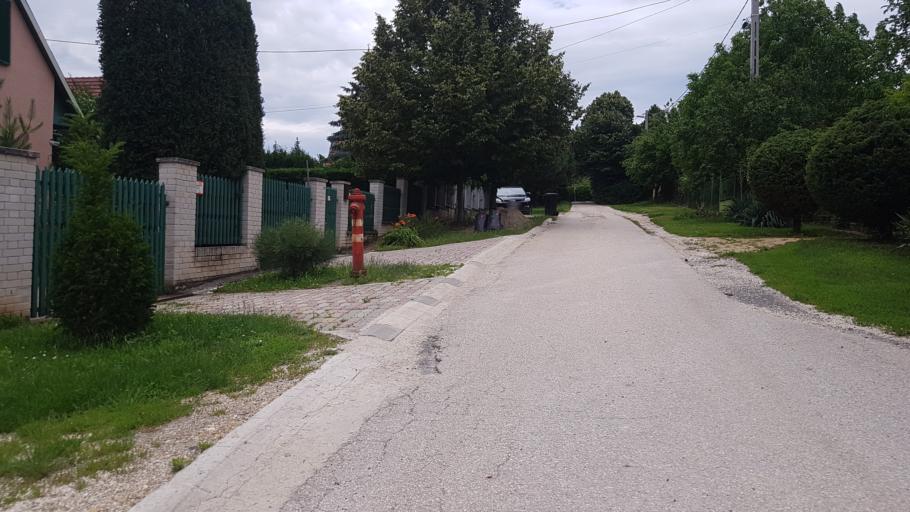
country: HU
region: Pest
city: Urom
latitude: 47.6142
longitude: 19.0166
